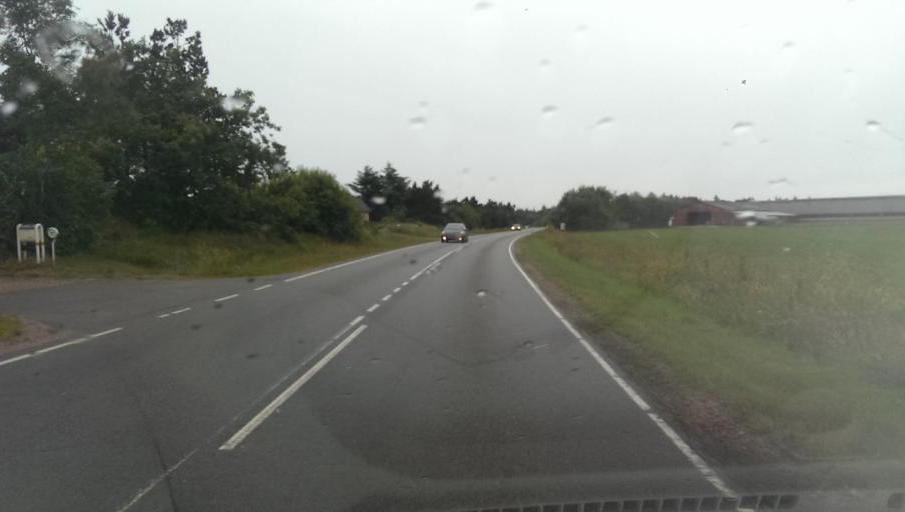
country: DK
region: South Denmark
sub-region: Varde Kommune
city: Oksbol
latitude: 55.8056
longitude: 8.2227
